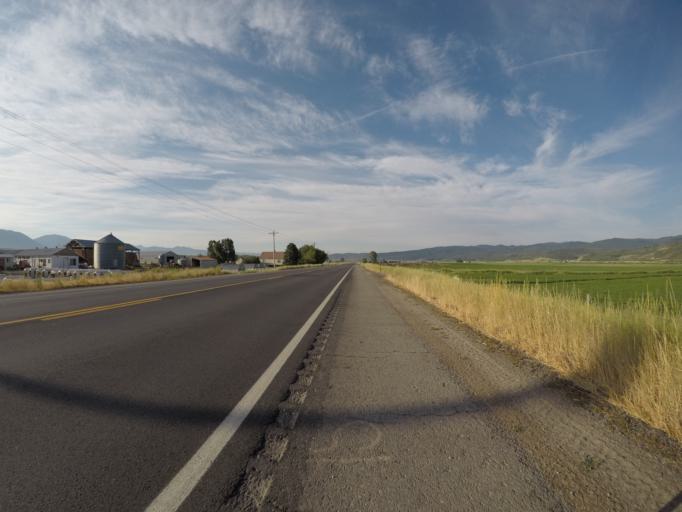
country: US
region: Wyoming
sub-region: Lincoln County
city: Afton
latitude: 42.9654
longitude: -111.0124
